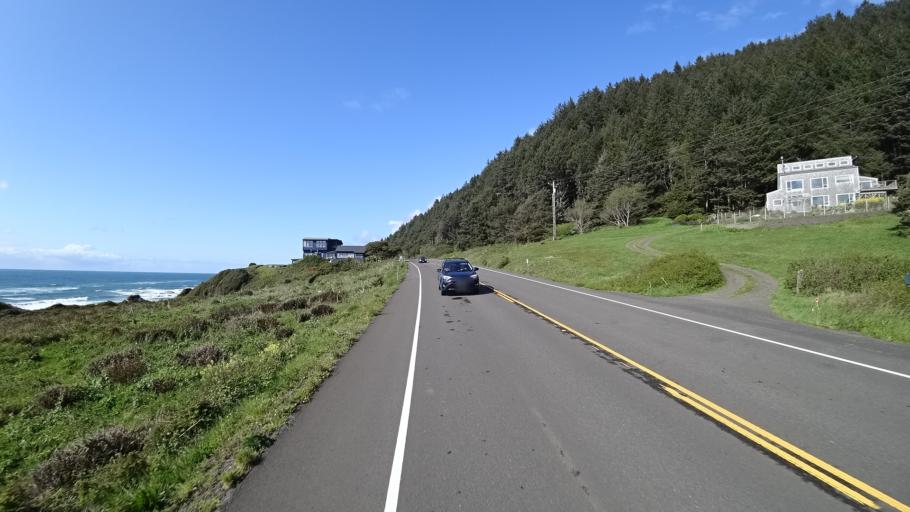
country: US
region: Oregon
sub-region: Lincoln County
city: Waldport
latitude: 44.2098
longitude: -124.1136
